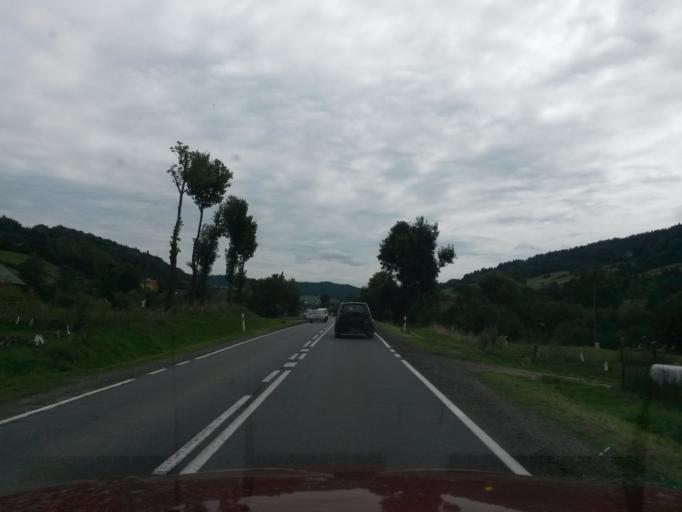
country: PL
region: Lesser Poland Voivodeship
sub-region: Powiat nowosadecki
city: Labowa
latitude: 49.5073
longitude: 20.8911
